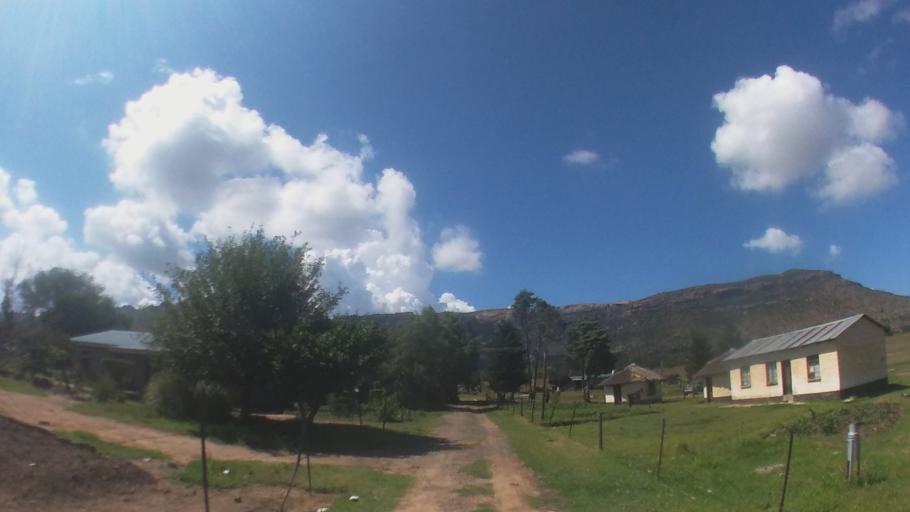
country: LS
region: Maseru
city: Nako
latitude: -29.6223
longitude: 27.5005
